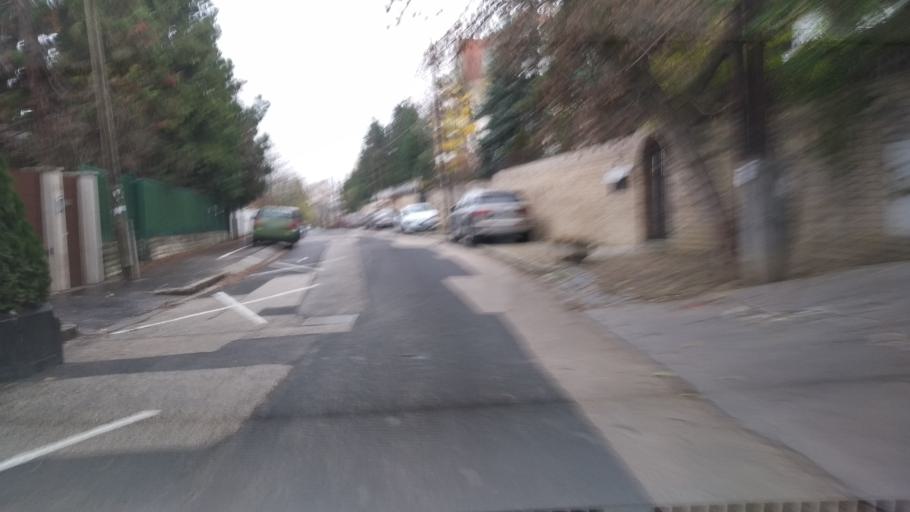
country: HU
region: Budapest
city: Budapest II. keruelet
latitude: 47.5218
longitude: 19.0103
